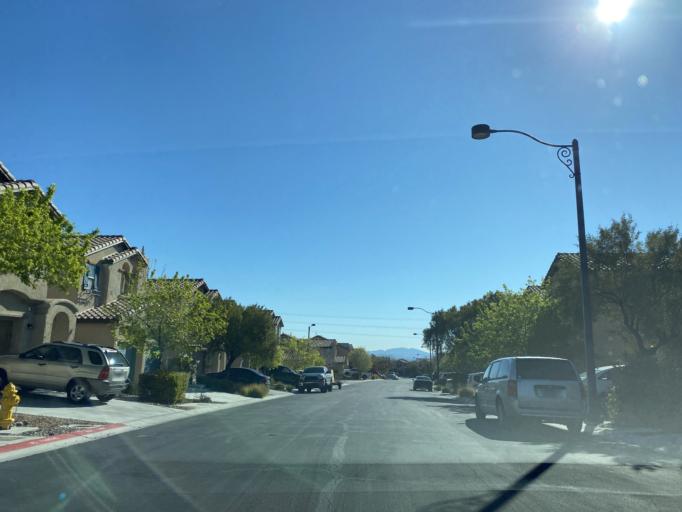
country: US
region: Nevada
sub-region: Clark County
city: Summerlin South
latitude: 36.3041
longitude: -115.3323
